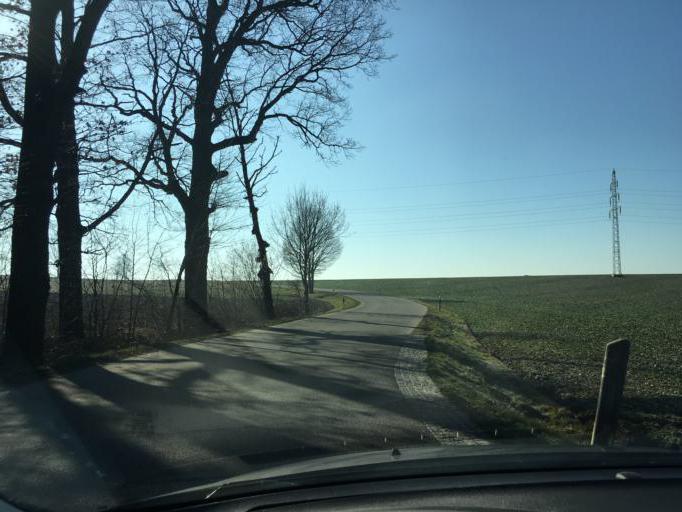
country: DE
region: Saxony
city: Narsdorf
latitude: 51.0258
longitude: 12.7101
